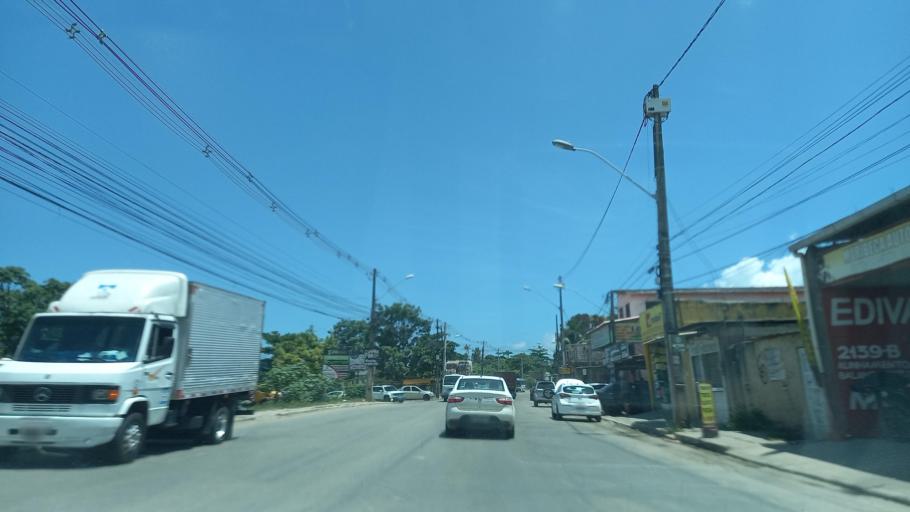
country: BR
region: Pernambuco
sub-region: Jaboatao Dos Guararapes
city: Jaboatao
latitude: -8.1540
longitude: -34.9587
